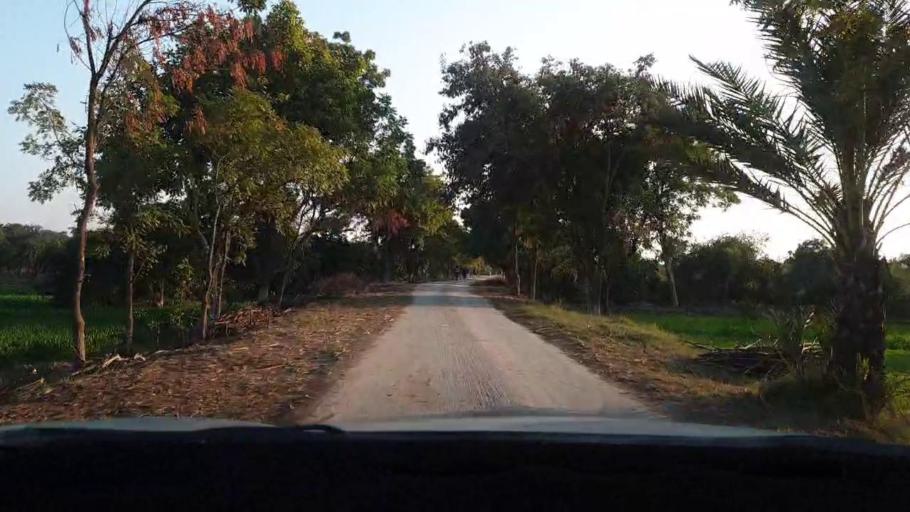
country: PK
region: Sindh
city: Berani
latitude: 25.7798
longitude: 68.7741
